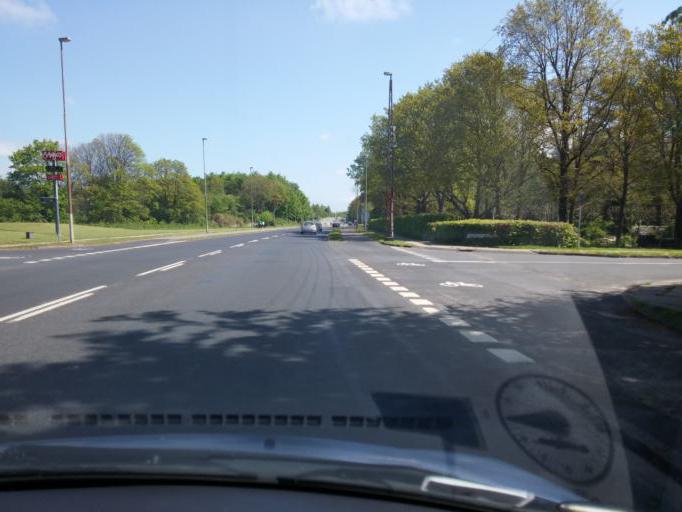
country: DK
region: South Denmark
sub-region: Odense Kommune
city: Stige
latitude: 55.4147
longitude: 10.4157
